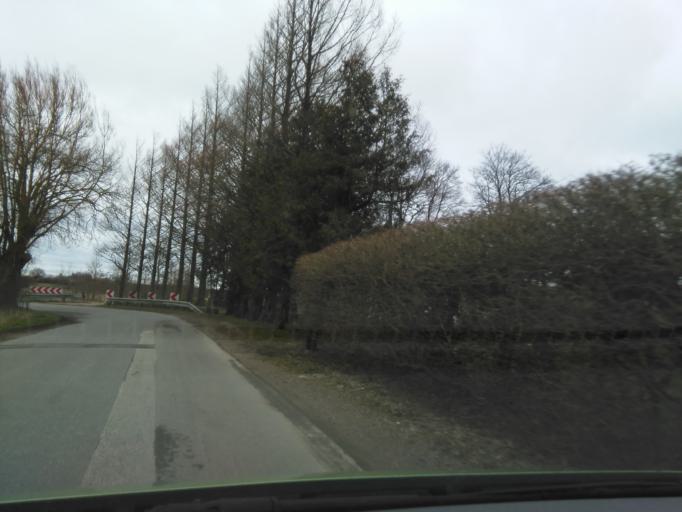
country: DK
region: Central Jutland
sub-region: Arhus Kommune
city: Beder
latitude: 56.0512
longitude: 10.2172
